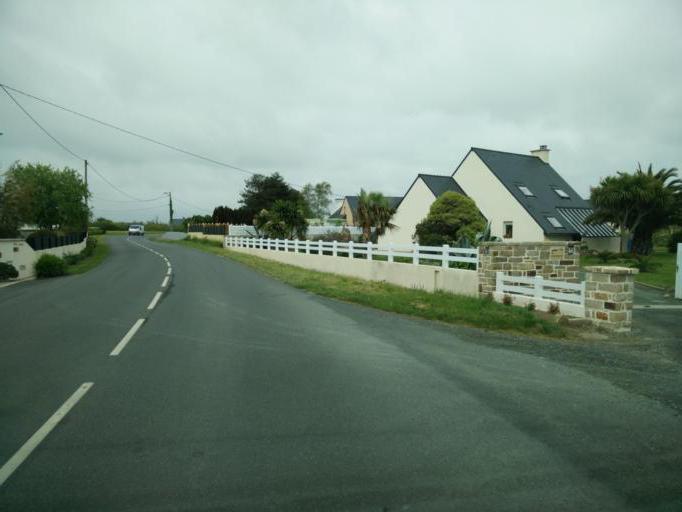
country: FR
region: Brittany
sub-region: Departement du Finistere
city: Loctudy
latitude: 47.8079
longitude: -4.1839
